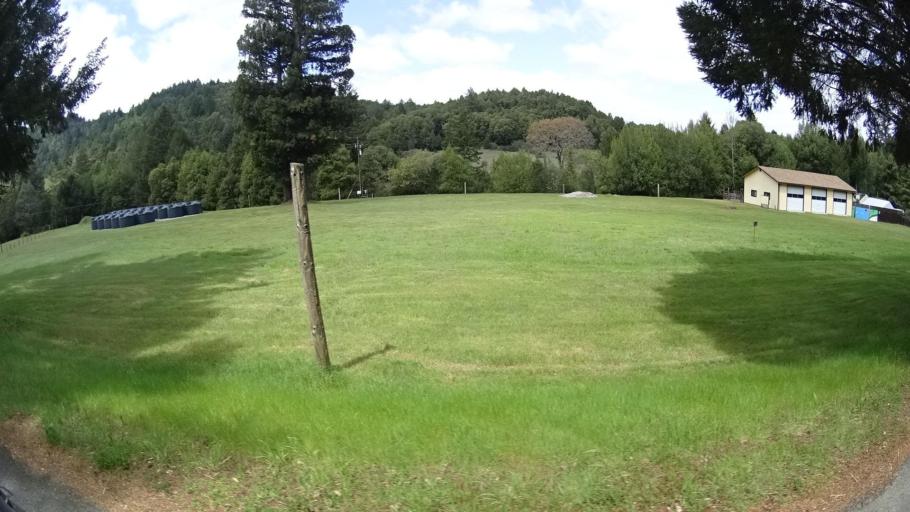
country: US
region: California
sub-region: Humboldt County
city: Redway
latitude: 40.0478
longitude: -123.9606
